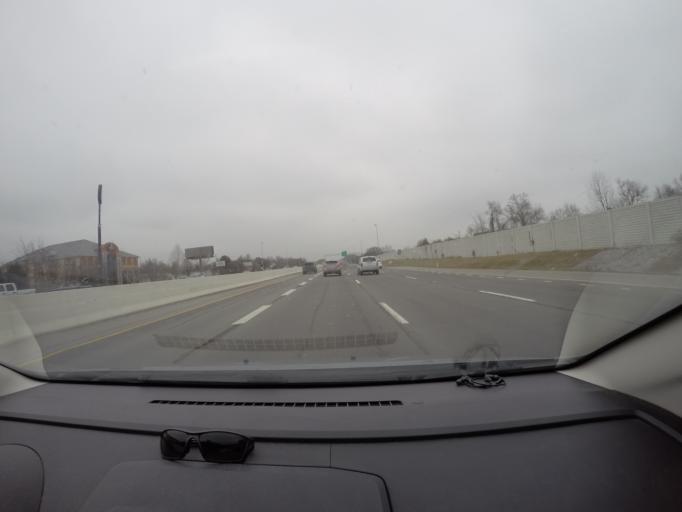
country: US
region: Tennessee
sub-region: Rutherford County
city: Murfreesboro
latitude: 35.8435
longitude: -86.4312
